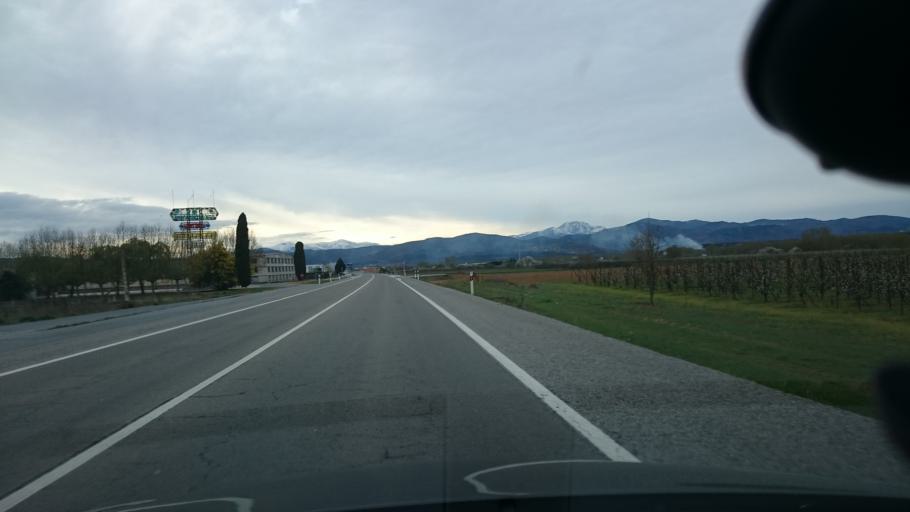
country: ES
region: Castille and Leon
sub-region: Provincia de Leon
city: Carracedelo
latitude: 42.5649
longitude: -6.7079
